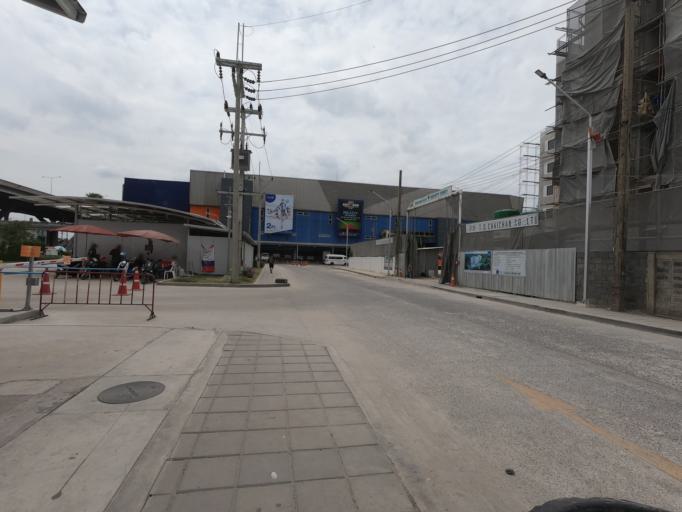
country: TH
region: Bangkok
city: Sai Mai
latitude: 13.9584
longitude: 100.6389
